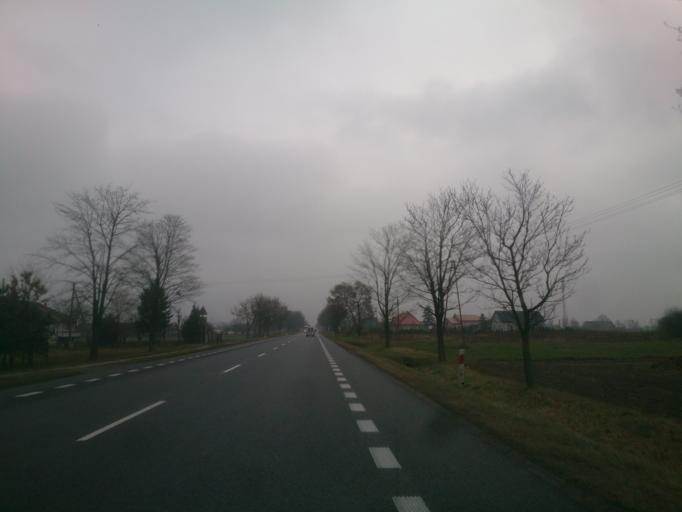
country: PL
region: Masovian Voivodeship
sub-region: Powiat sierpecki
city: Zawidz
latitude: 52.8141
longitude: 19.7997
